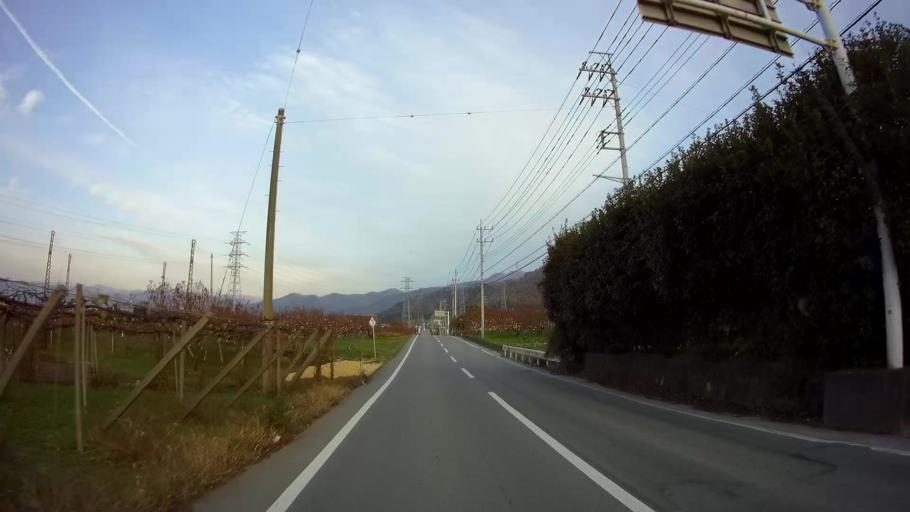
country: JP
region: Yamanashi
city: Isawa
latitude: 35.6129
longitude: 138.6657
